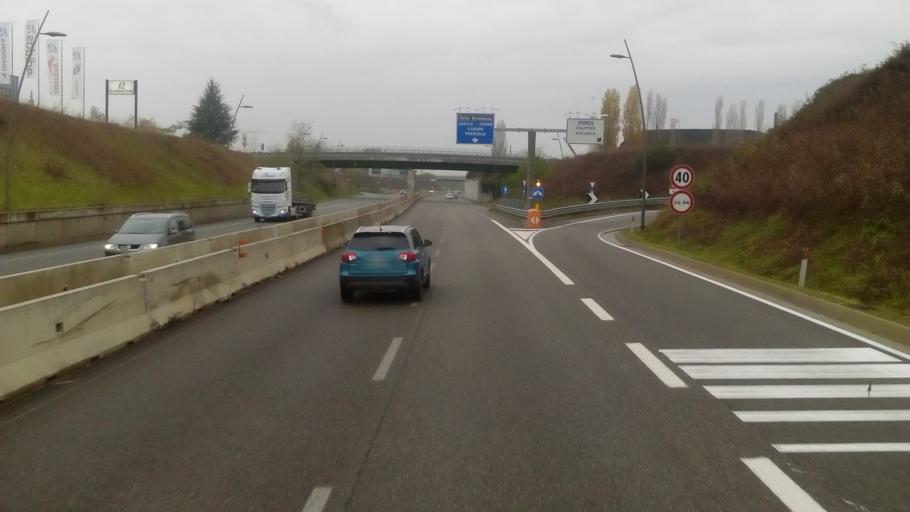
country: IT
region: Lombardy
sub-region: Provincia di Bergamo
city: Lallio
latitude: 45.6554
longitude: 9.6165
